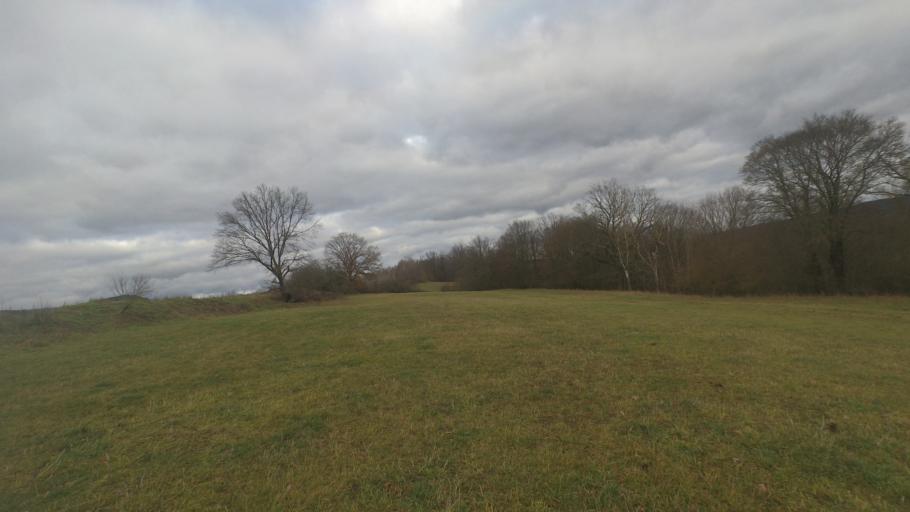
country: DE
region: Thuringia
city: Orlamunde
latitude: 50.7607
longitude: 11.5064
